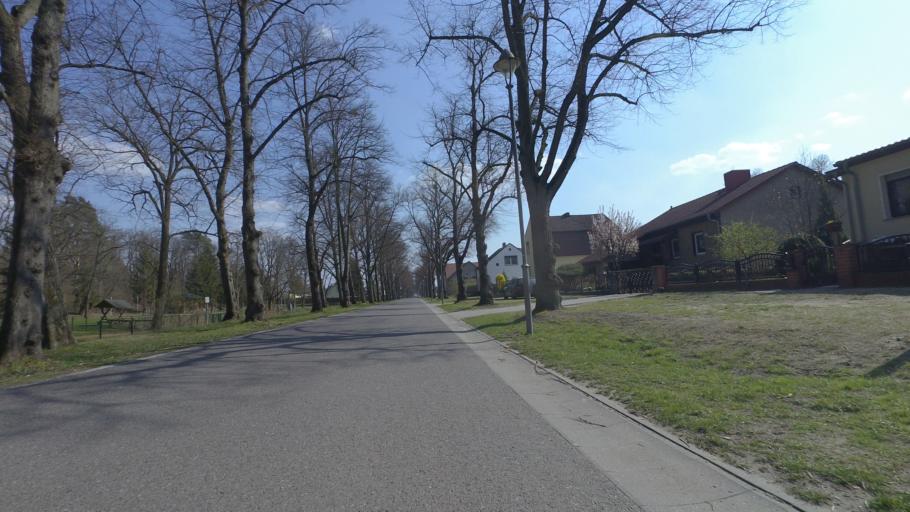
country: DE
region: Brandenburg
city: Teupitz
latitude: 52.1754
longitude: 13.5708
